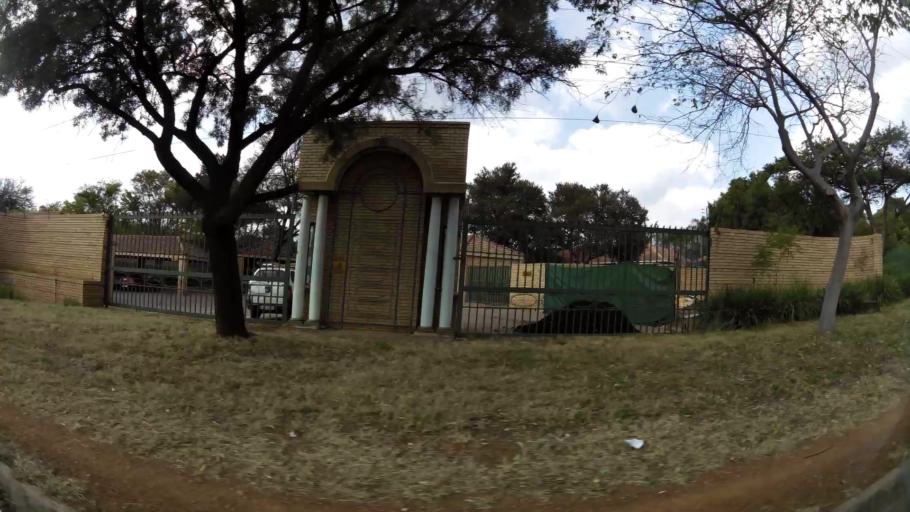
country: ZA
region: Gauteng
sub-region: City of Tshwane Metropolitan Municipality
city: Pretoria
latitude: -25.7806
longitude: 28.2874
